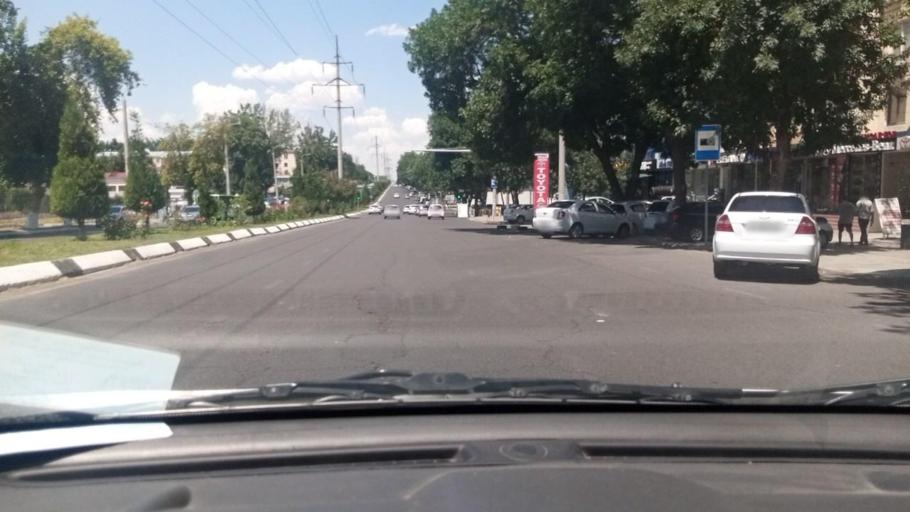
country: UZ
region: Toshkent Shahri
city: Tashkent
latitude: 41.2854
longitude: 69.1947
